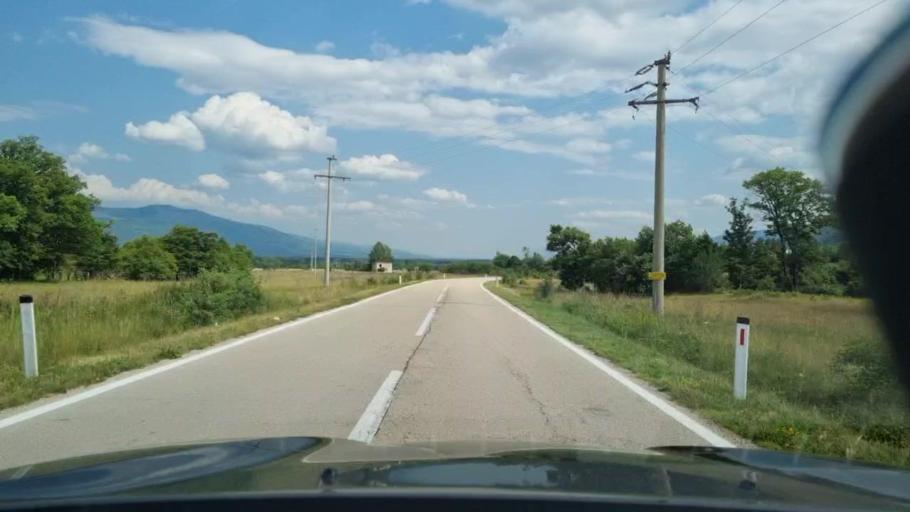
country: BA
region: Federation of Bosnia and Herzegovina
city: Bosansko Grahovo
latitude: 44.0878
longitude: 16.5663
